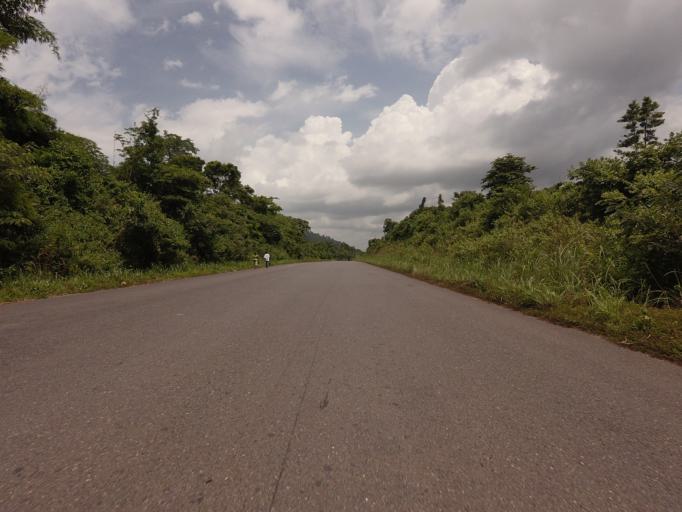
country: GH
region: Volta
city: Ho
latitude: 6.4851
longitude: 0.1979
